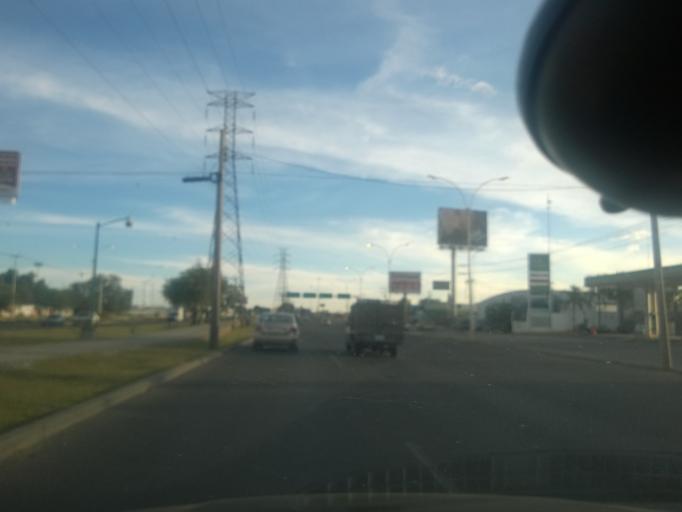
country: MX
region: Guanajuato
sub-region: Leon
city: Medina
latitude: 21.1308
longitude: -101.6300
